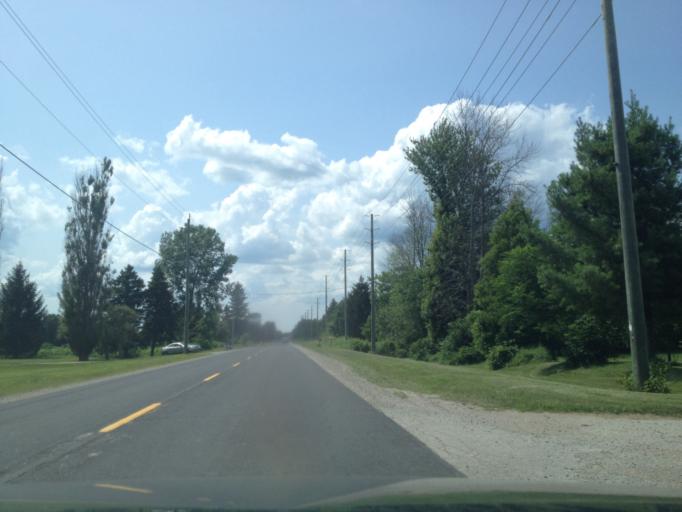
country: CA
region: Ontario
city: Aylmer
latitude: 42.6654
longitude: -80.8259
